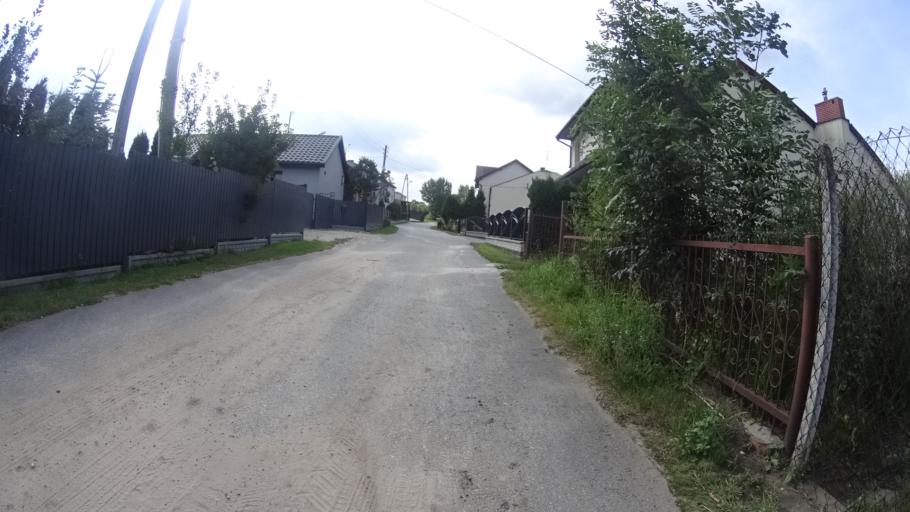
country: PL
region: Masovian Voivodeship
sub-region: Powiat grojecki
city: Mogielnica
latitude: 51.6575
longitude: 20.7592
